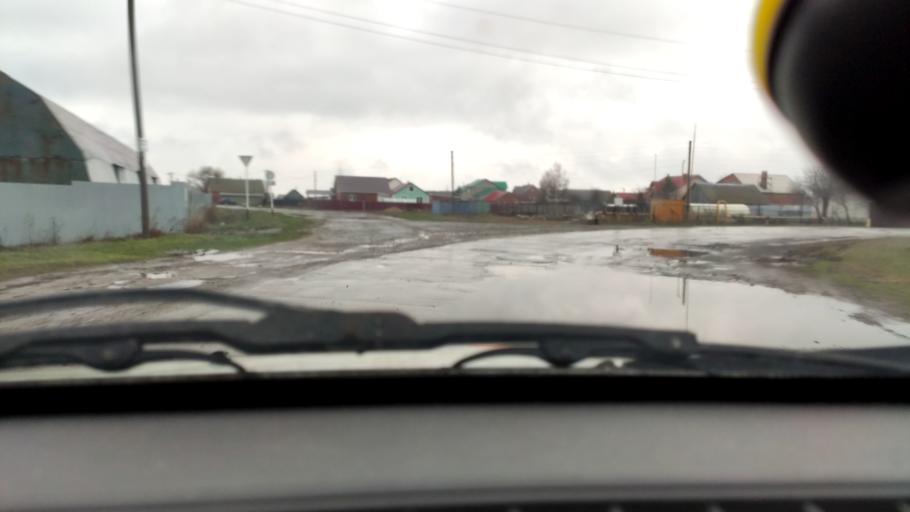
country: RU
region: Samara
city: Povolzhskiy
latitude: 53.6472
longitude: 49.6869
